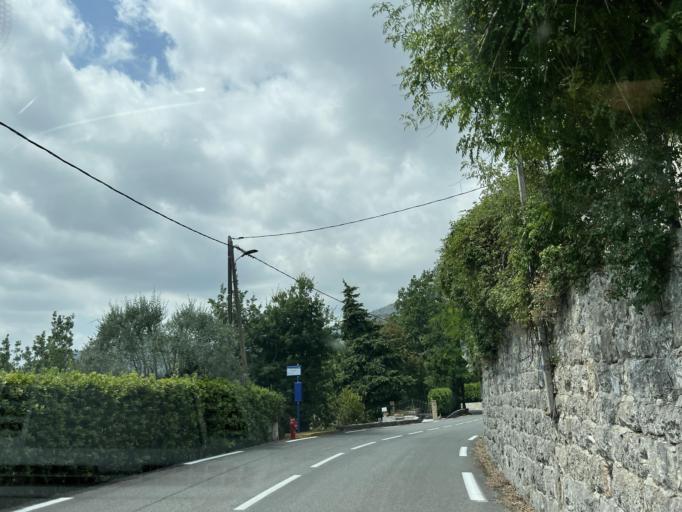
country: FR
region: Provence-Alpes-Cote d'Azur
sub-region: Departement des Alpes-Maritimes
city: Le Rouret
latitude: 43.7048
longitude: 7.0106
